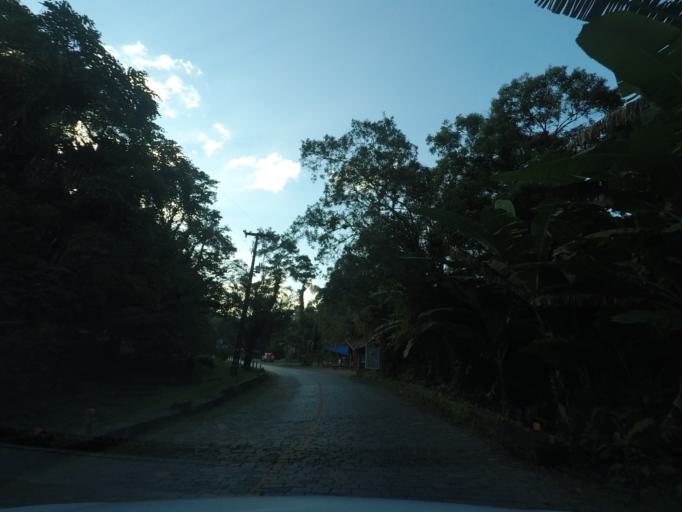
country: BR
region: Parana
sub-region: Antonina
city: Antonina
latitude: -25.3647
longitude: -48.8746
